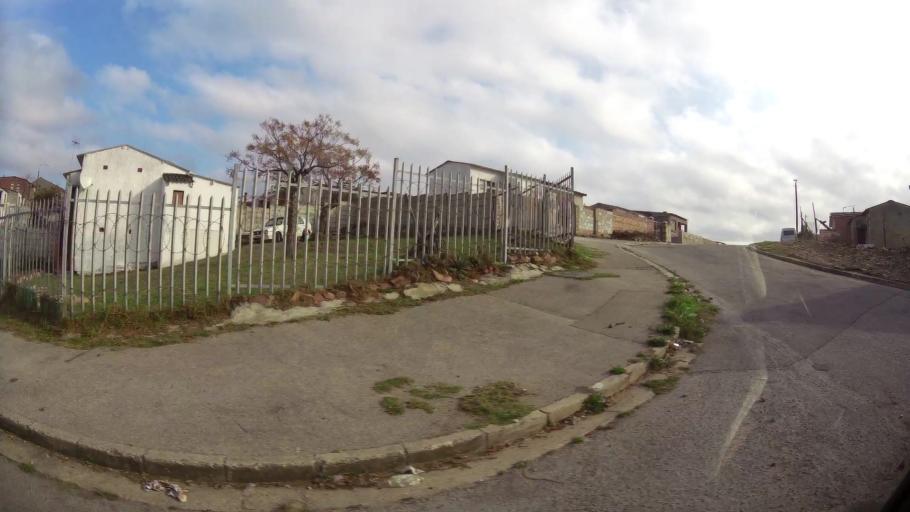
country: ZA
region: Eastern Cape
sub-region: Nelson Mandela Bay Metropolitan Municipality
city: Port Elizabeth
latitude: -33.9196
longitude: 25.5468
